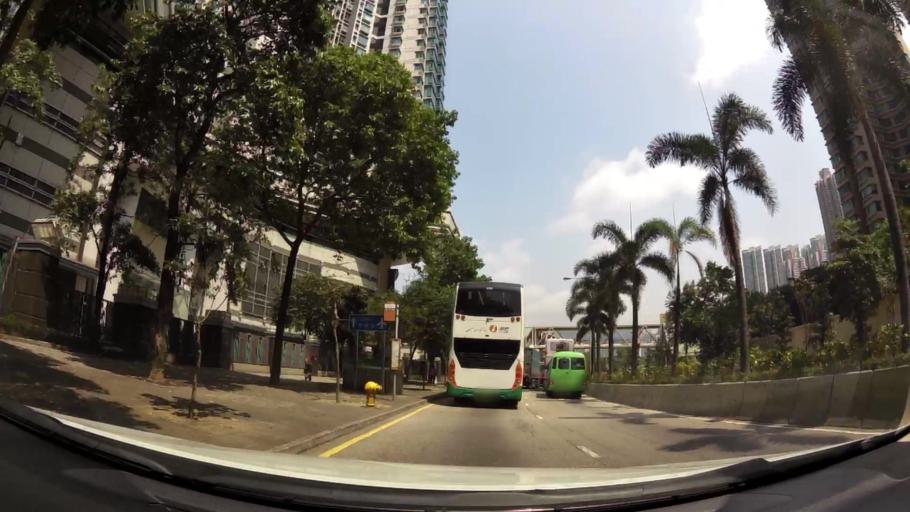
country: HK
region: Sham Shui Po
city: Sham Shui Po
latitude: 22.3195
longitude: 114.1565
